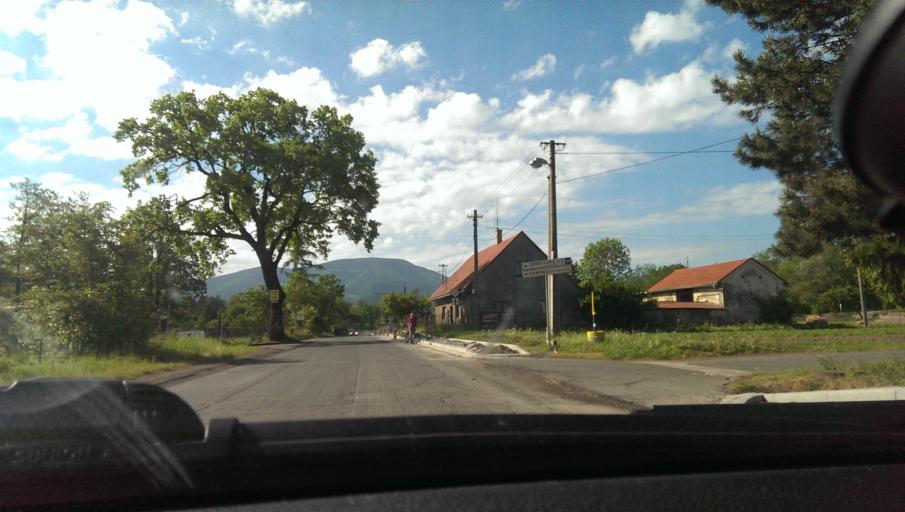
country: CZ
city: Frydlant nad Ostravici
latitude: 49.5788
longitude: 18.3585
